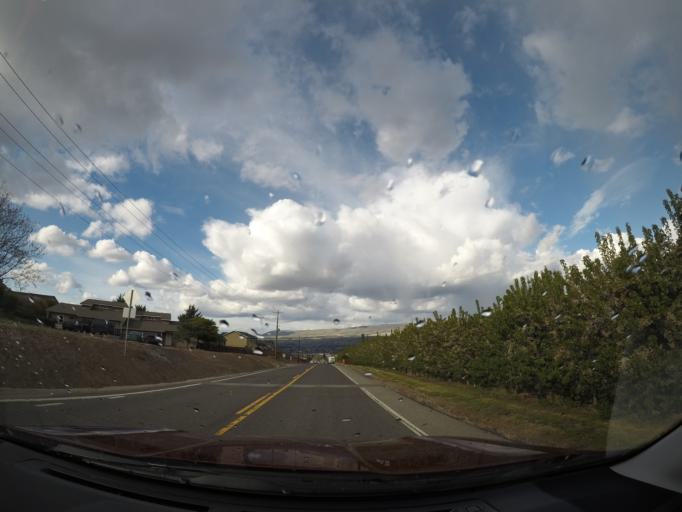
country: US
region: Washington
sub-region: Chelan County
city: South Wenatchee
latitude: 47.3869
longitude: -120.3087
